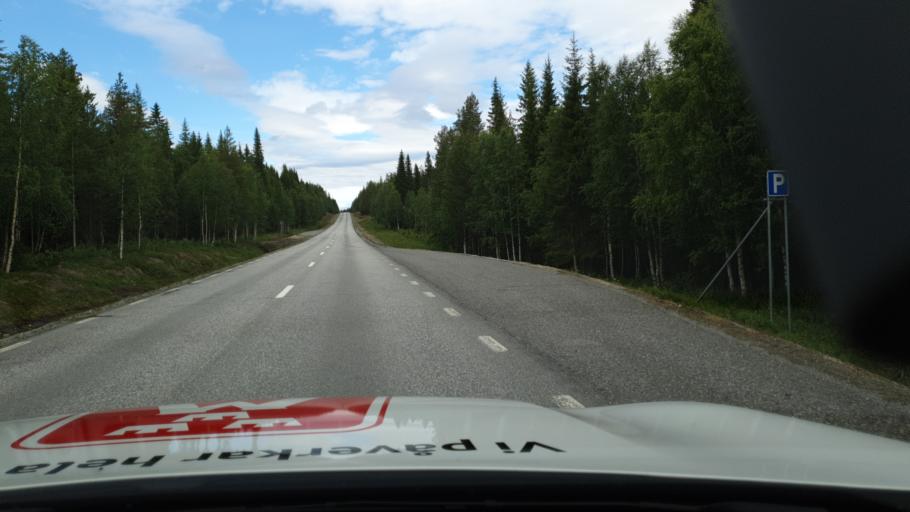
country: SE
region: Vaesterbotten
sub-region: Storumans Kommun
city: Fristad
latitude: 65.3408
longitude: 16.6095
